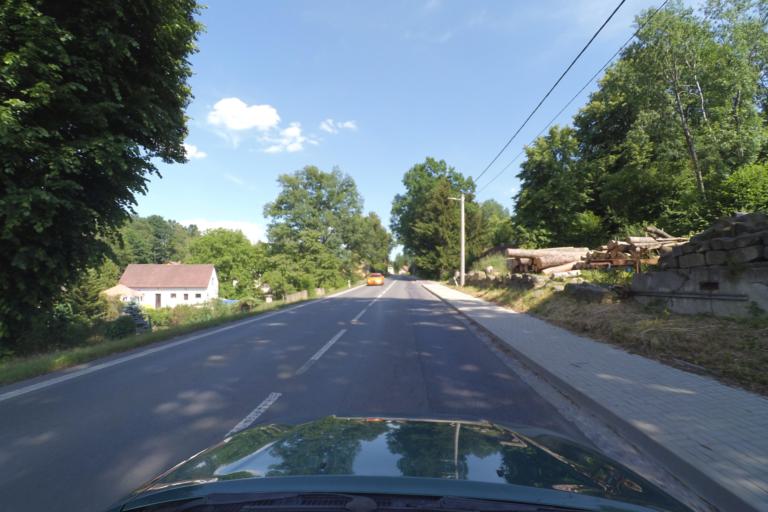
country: CZ
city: Zakupy
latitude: 50.6694
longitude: 14.6767
